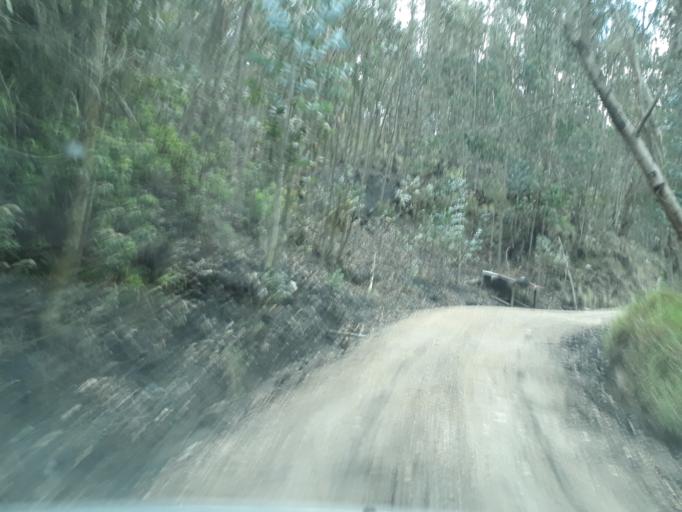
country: CO
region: Cundinamarca
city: Lenguazaque
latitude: 5.2682
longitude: -73.6929
